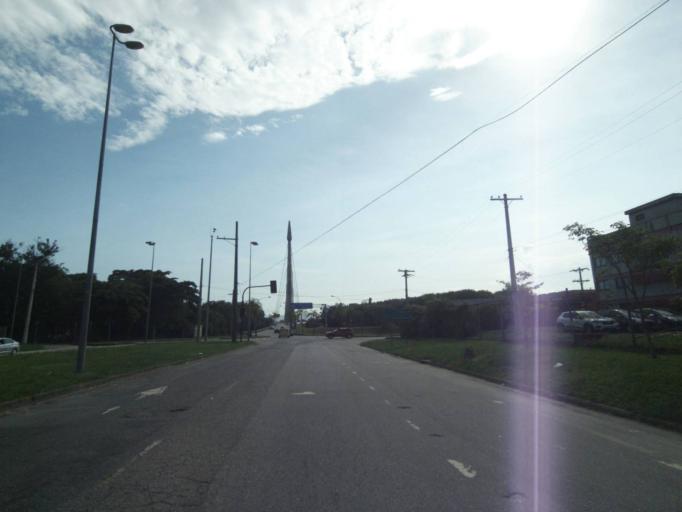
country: BR
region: Rio de Janeiro
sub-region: Rio De Janeiro
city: Rio de Janeiro
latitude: -22.8642
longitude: -43.2286
